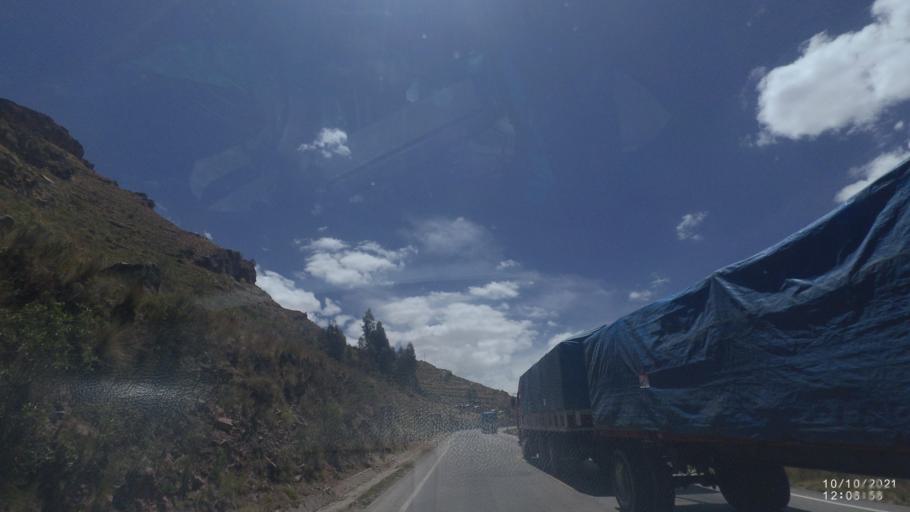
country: BO
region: Cochabamba
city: Irpa Irpa
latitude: -17.7156
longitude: -66.5556
